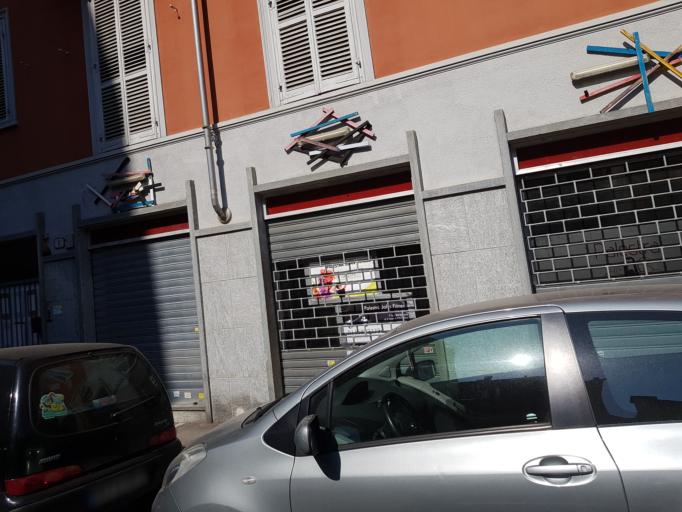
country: IT
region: Piedmont
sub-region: Provincia di Torino
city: Lesna
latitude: 45.0626
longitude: 7.6491
